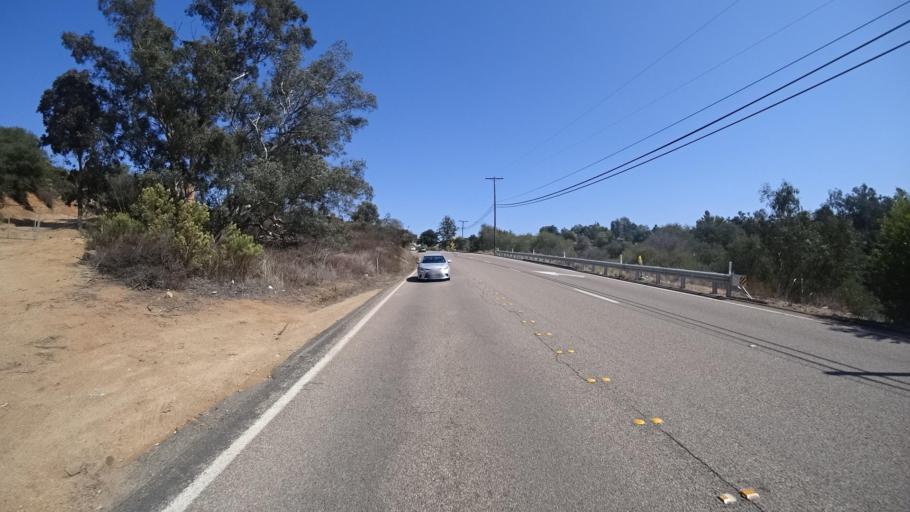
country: US
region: California
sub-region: San Diego County
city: Crest
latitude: 32.8148
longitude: -116.8662
